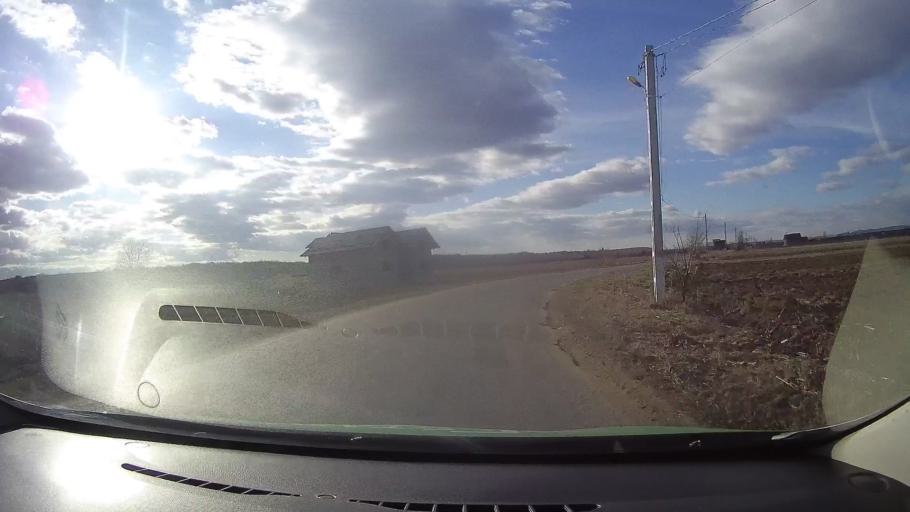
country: RO
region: Dambovita
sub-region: Comuna Ulmi
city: Ulmi
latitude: 44.8948
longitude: 25.5019
